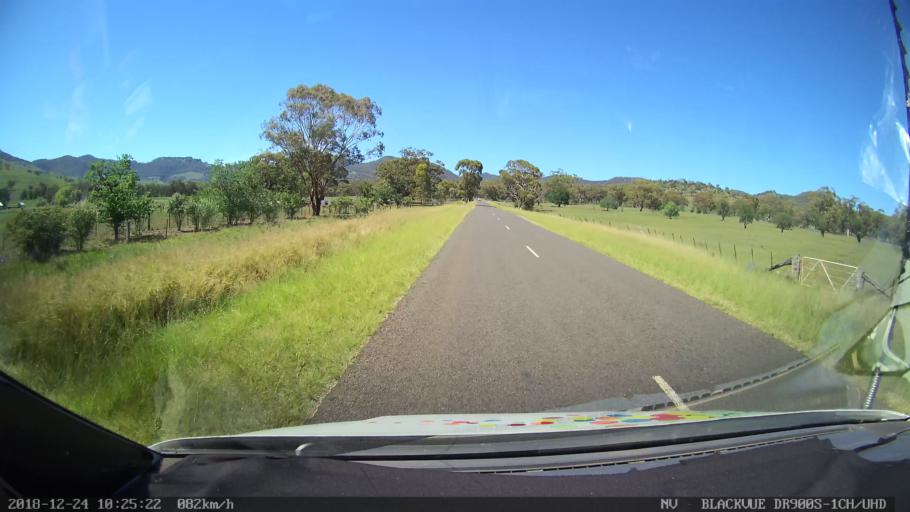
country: AU
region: New South Wales
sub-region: Liverpool Plains
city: Quirindi
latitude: -31.7980
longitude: 150.5288
